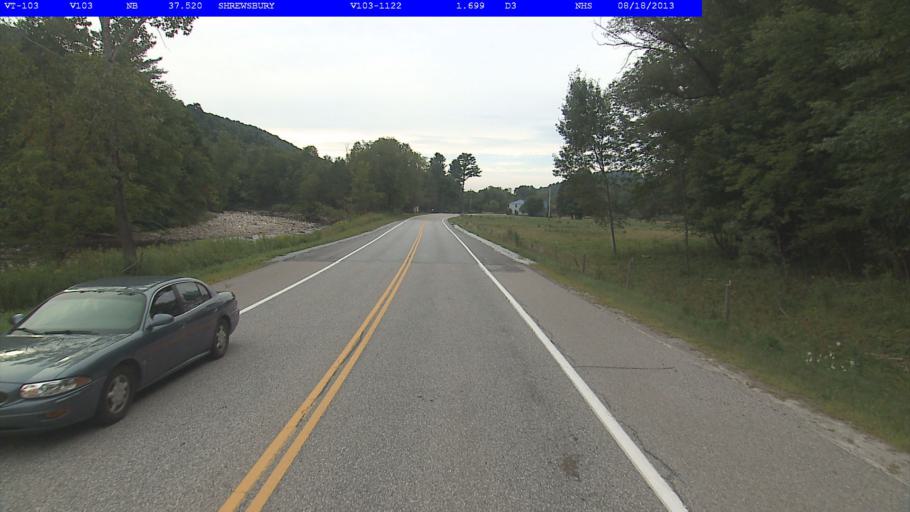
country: US
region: Vermont
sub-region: Rutland County
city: Rutland
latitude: 43.4987
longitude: -72.8955
